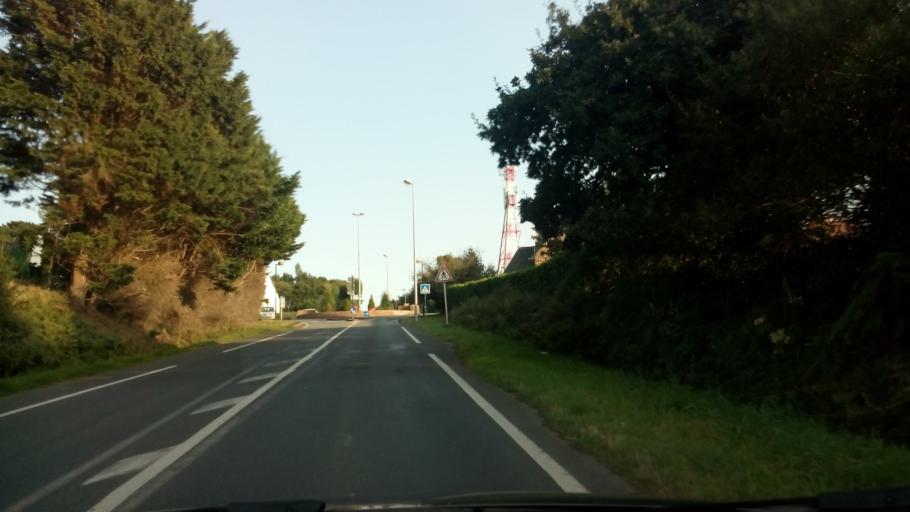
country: FR
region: Brittany
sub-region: Departement des Cotes-d'Armor
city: Pleumeur-Bodou
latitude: 48.7739
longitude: -3.5214
